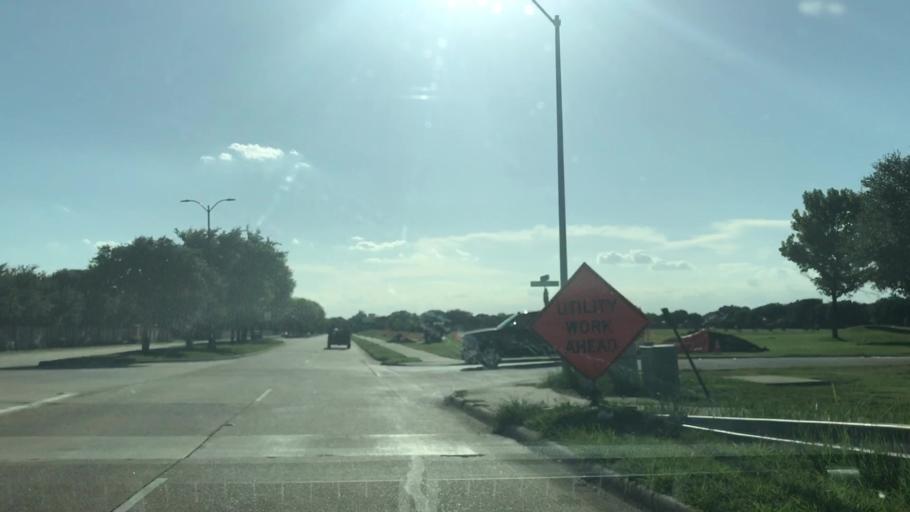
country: US
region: Texas
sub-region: Collin County
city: Frisco
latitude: 33.1161
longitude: -96.7809
